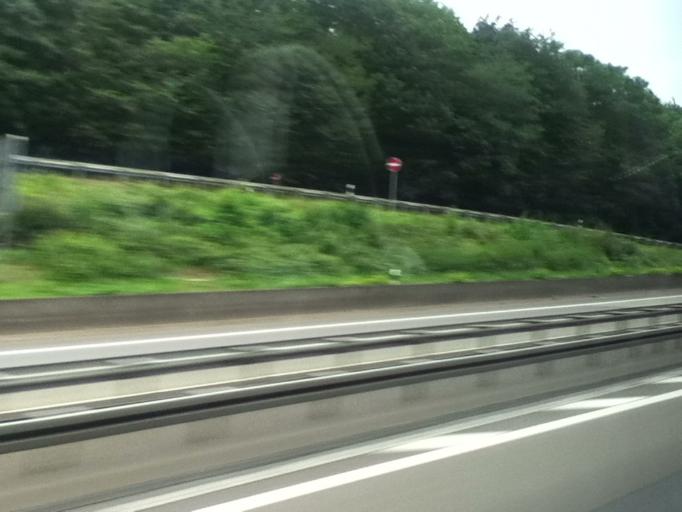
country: DE
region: North Rhine-Westphalia
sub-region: Regierungsbezirk Koln
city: Rath
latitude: 50.9479
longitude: 7.0989
